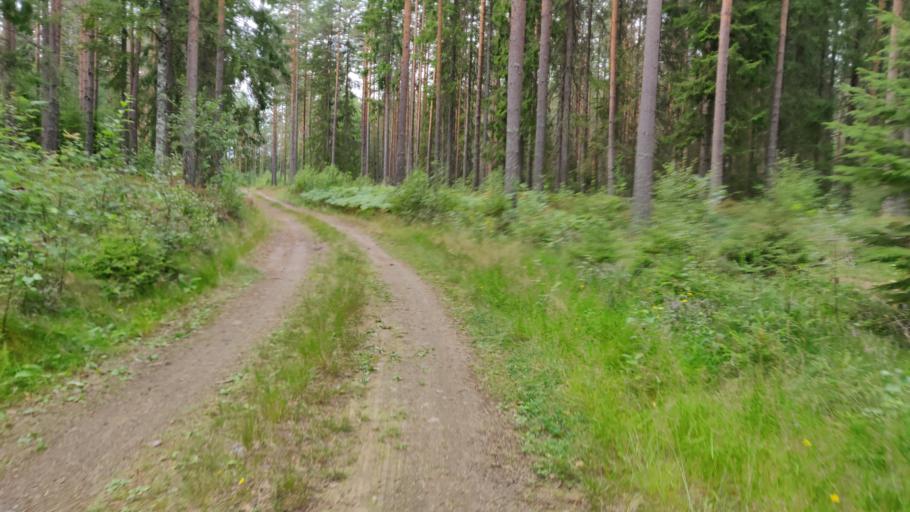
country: SE
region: Vaermland
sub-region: Hagfors Kommun
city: Hagfors
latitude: 60.0143
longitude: 13.5619
